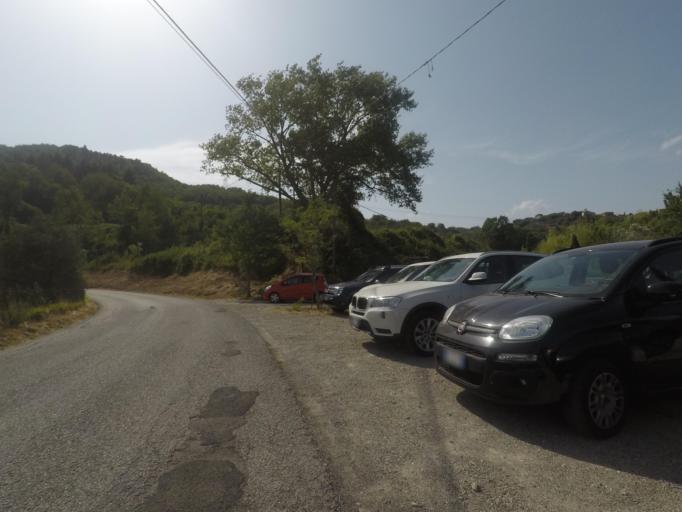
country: IT
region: Tuscany
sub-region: Provincia di Massa-Carrara
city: Fivizzano
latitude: 44.1695
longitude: 10.1043
